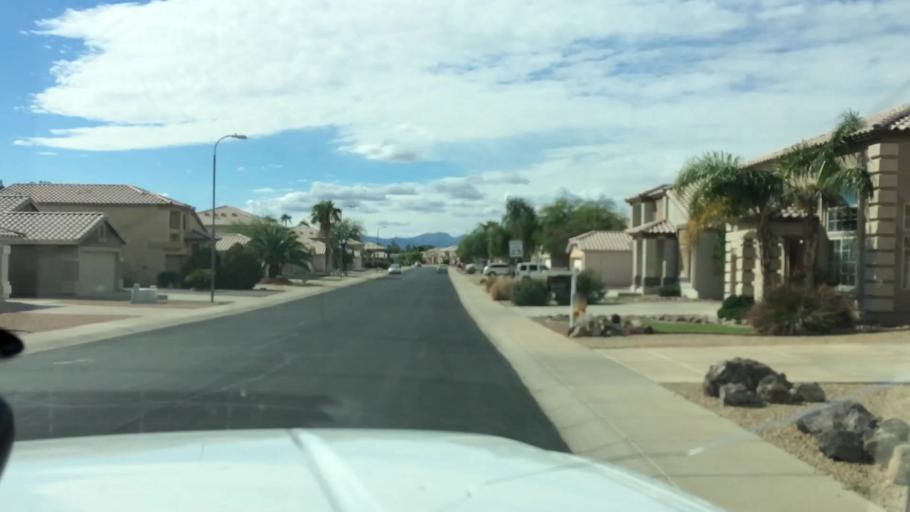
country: US
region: Arizona
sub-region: Maricopa County
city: Peoria
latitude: 33.5683
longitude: -112.2641
